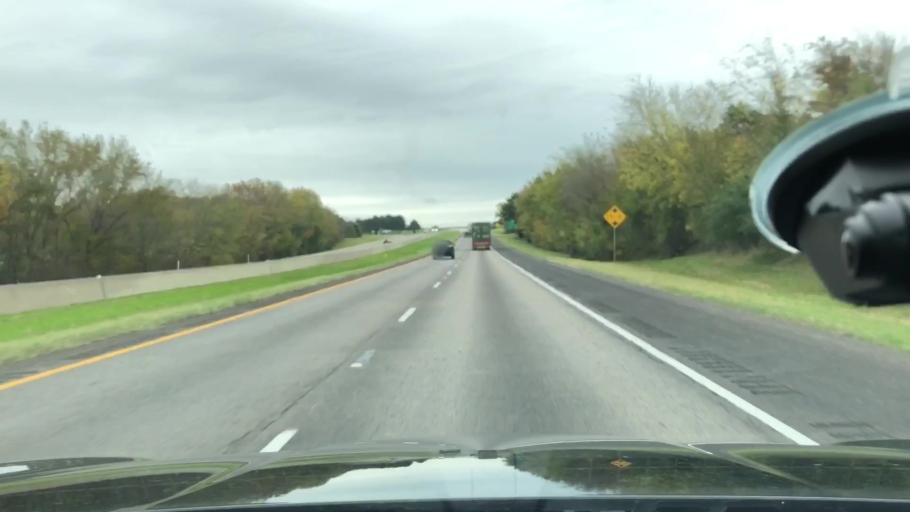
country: US
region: Texas
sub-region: Hopkins County
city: Sulphur Springs
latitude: 33.1593
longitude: -95.4135
